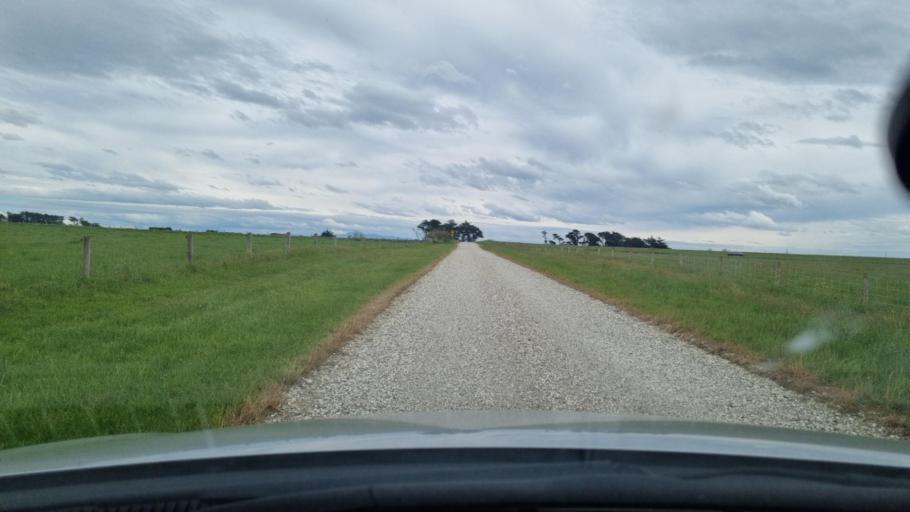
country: NZ
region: Southland
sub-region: Invercargill City
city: Invercargill
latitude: -46.3985
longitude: 168.2644
